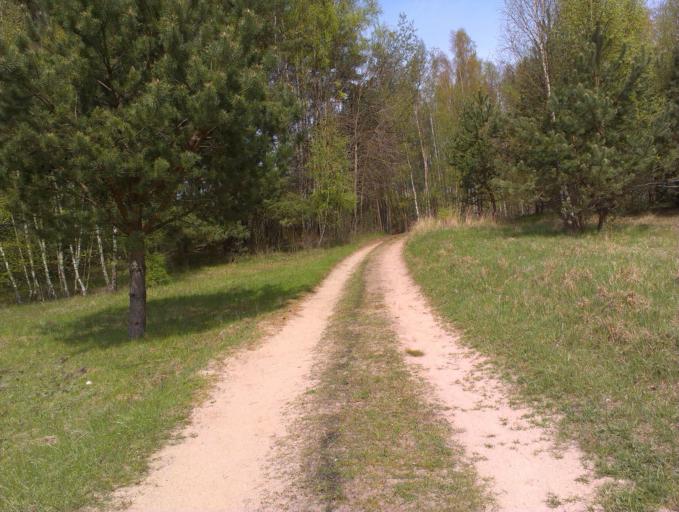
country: PL
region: West Pomeranian Voivodeship
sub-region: Powiat szczecinecki
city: Lubowo
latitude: 53.6249
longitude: 16.3497
